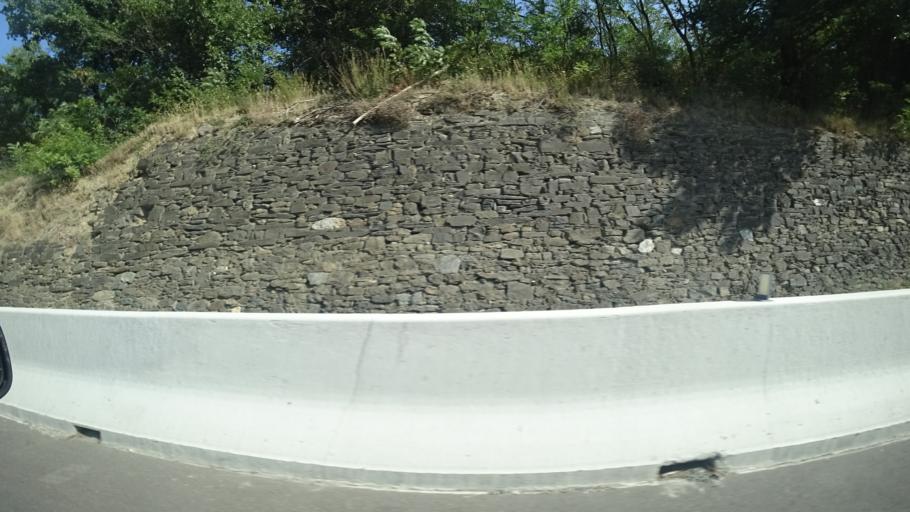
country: FR
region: Languedoc-Roussillon
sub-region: Departement des Pyrenees-Orientales
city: Vernet-les-Bains
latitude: 42.5612
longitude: 2.2982
